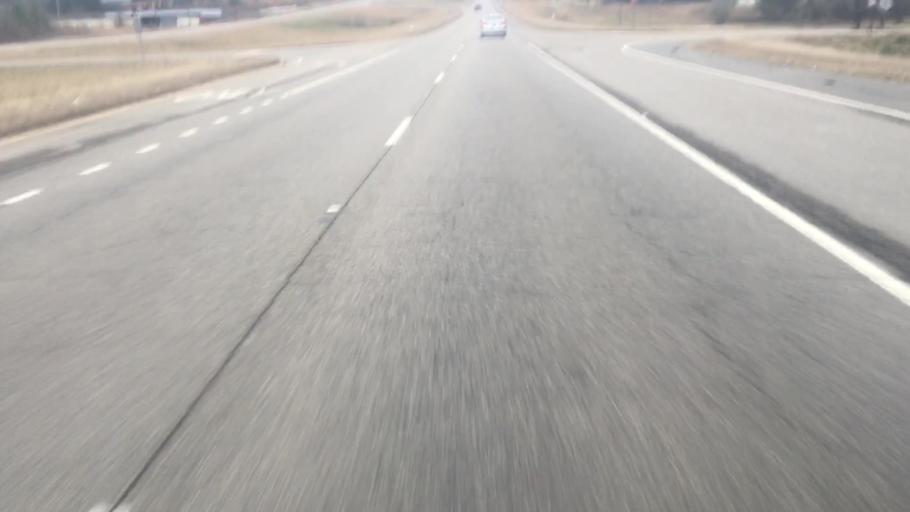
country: US
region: Alabama
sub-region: Walker County
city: Cordova
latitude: 33.8045
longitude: -87.1304
